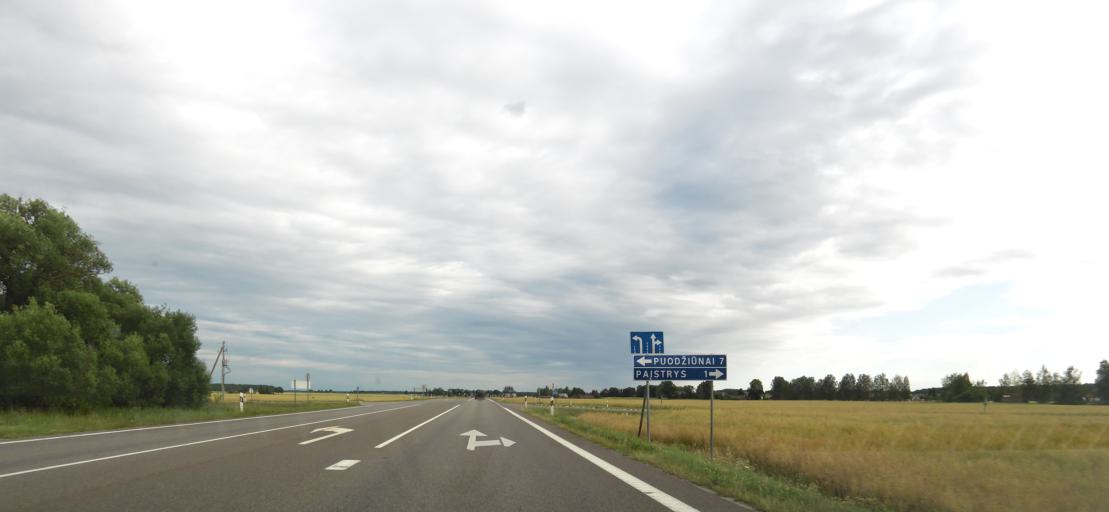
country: LT
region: Panevezys
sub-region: Panevezys City
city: Panevezys
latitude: 55.8568
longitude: 24.3500
